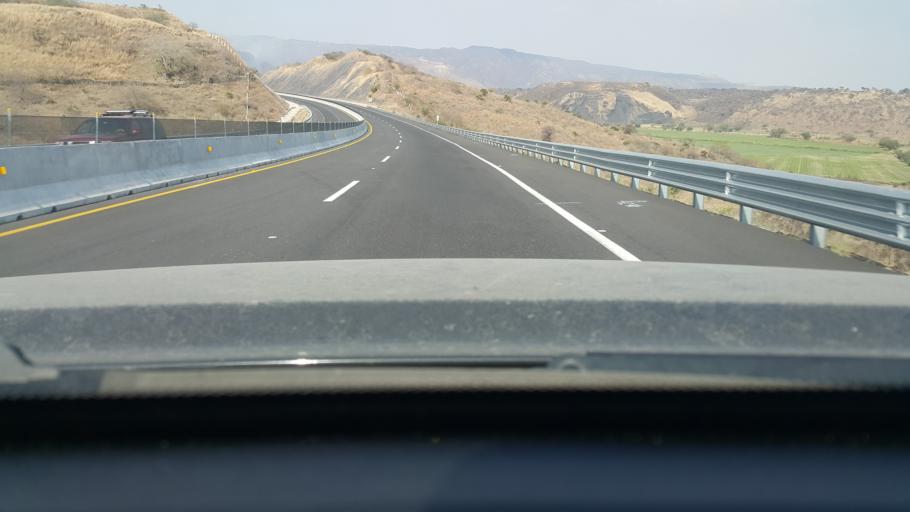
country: MX
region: Nayarit
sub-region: Ahuacatlan
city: Ahuacatlan
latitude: 21.0676
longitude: -104.4637
